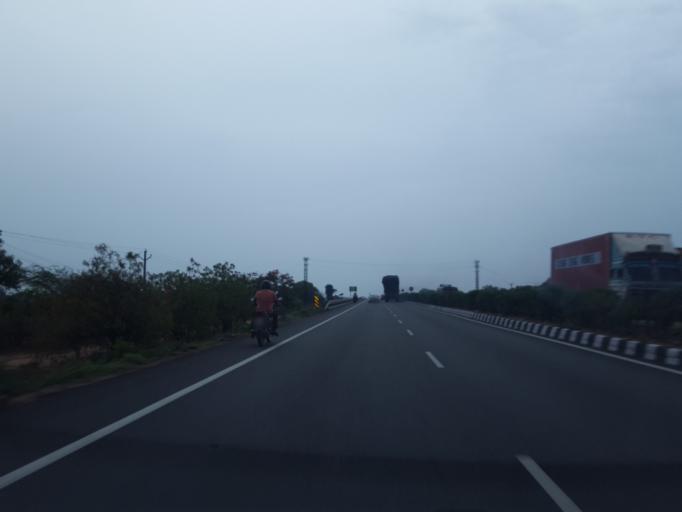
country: IN
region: Telangana
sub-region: Mahbubnagar
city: Farrukhnagar
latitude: 17.0780
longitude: 78.2284
